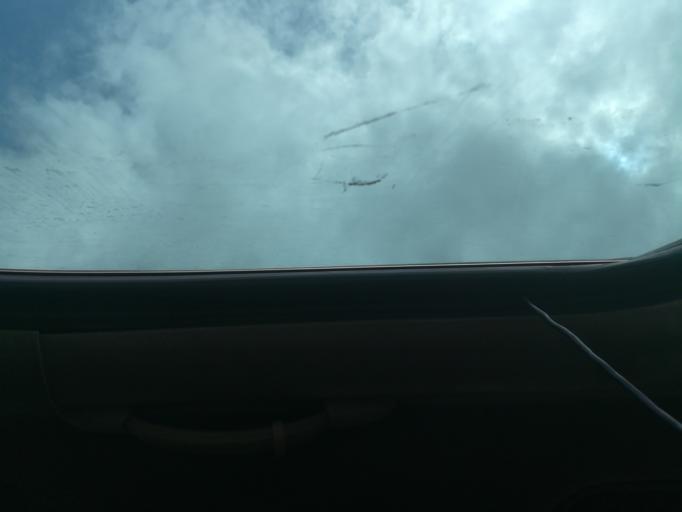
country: NG
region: Lagos
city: Lagos
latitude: 6.4128
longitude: 3.4120
